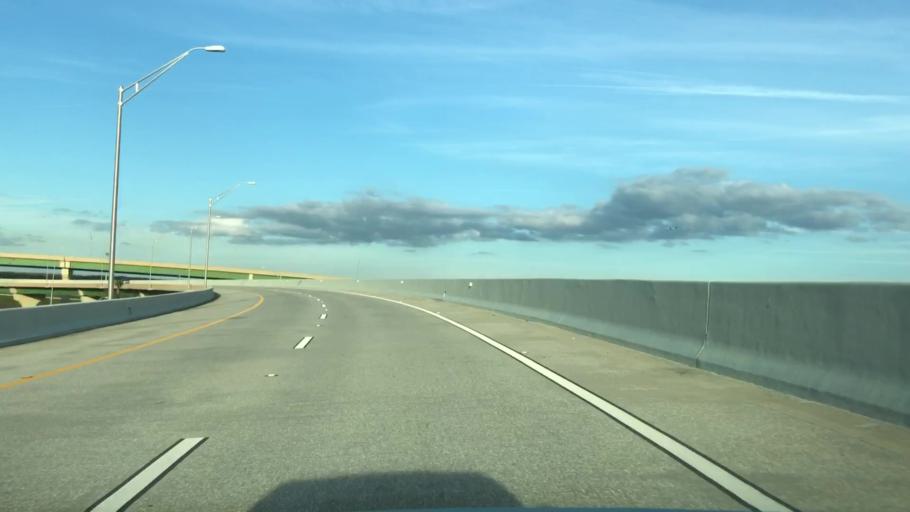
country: US
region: Florida
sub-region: Osceola County
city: Buenaventura Lakes
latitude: 28.3682
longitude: -81.3103
